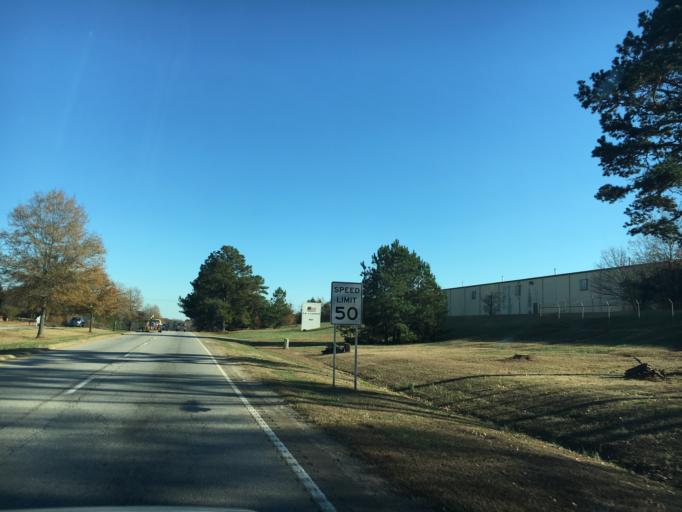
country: US
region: South Carolina
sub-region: Spartanburg County
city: Wellford
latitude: 34.9451
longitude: -82.0916
